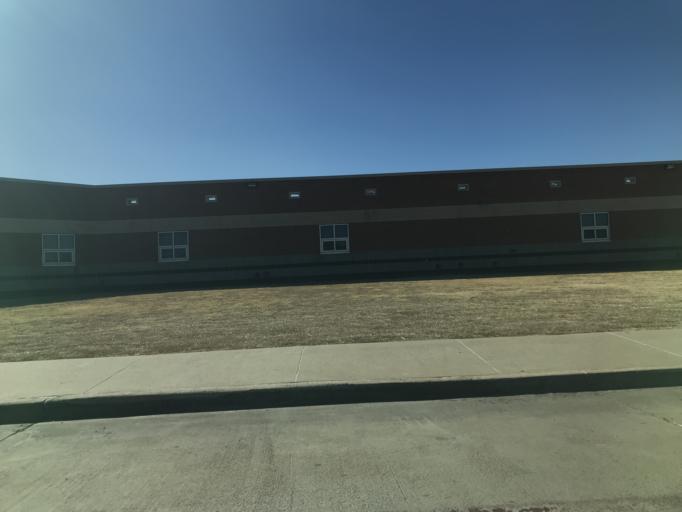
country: US
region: Texas
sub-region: Taylor County
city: Abilene
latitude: 32.4421
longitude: -99.7071
